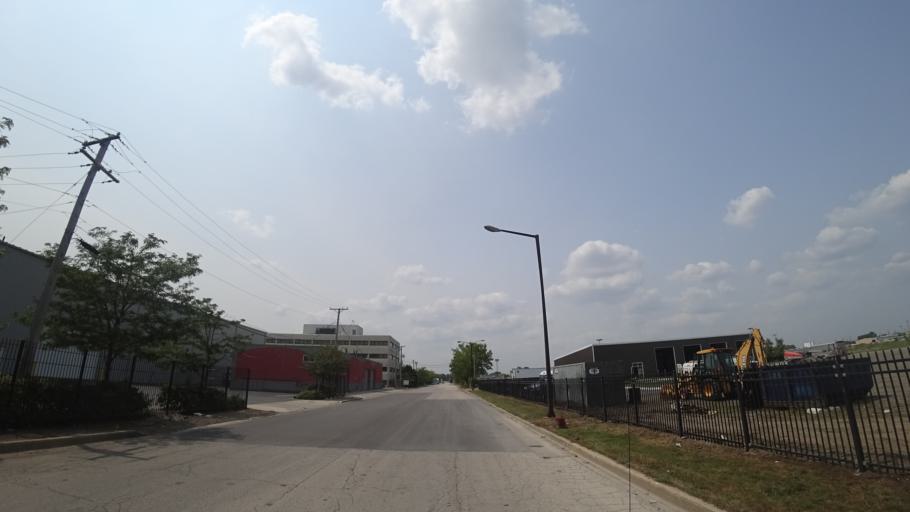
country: US
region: Illinois
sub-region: Cook County
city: Cicero
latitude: 41.8272
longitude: -87.7304
